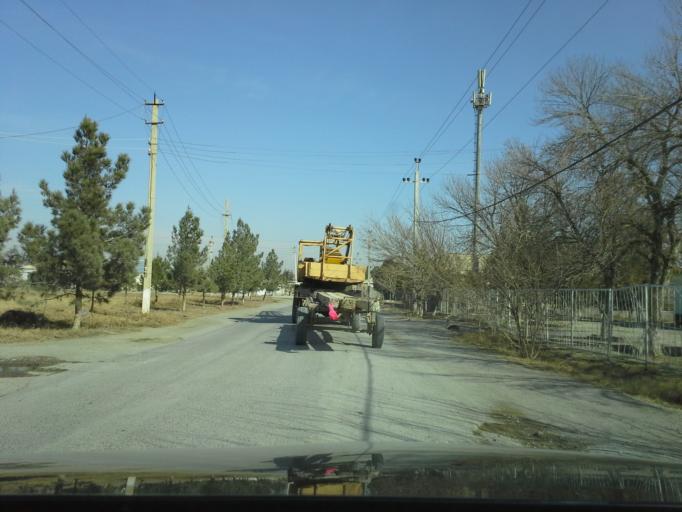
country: TM
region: Ahal
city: Abadan
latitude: 38.1238
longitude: 57.9975
